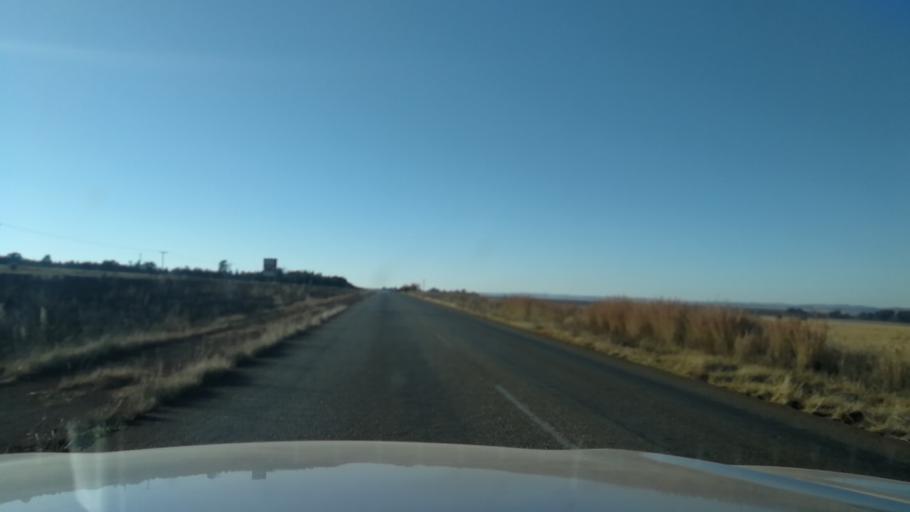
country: ZA
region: North-West
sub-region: Bojanala Platinum District Municipality
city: Koster
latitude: -25.9383
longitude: 27.1527
